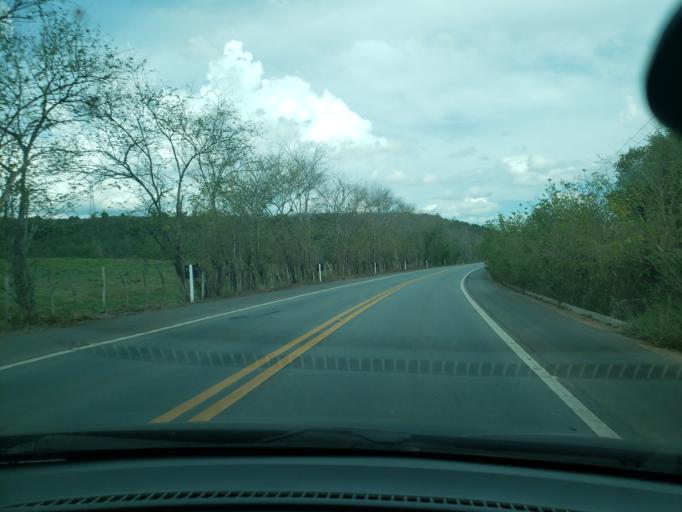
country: BR
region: Alagoas
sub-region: Murici
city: Murici
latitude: -9.2576
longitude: -35.9786
